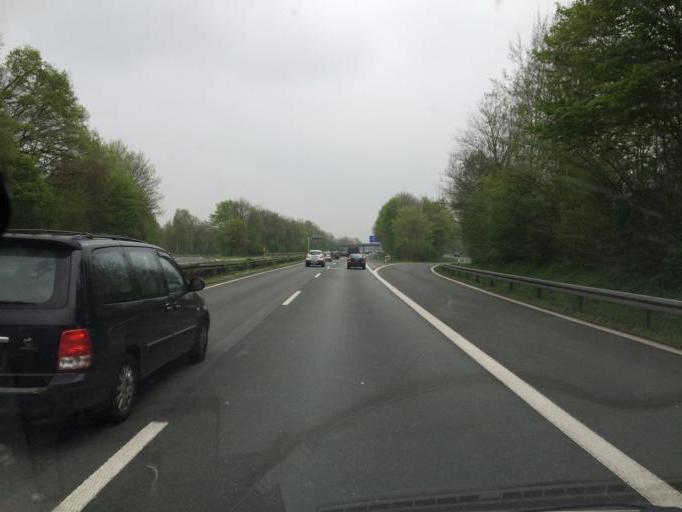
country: DE
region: North Rhine-Westphalia
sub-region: Regierungsbezirk Munster
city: Recklinghausen
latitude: 51.6409
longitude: 7.1712
